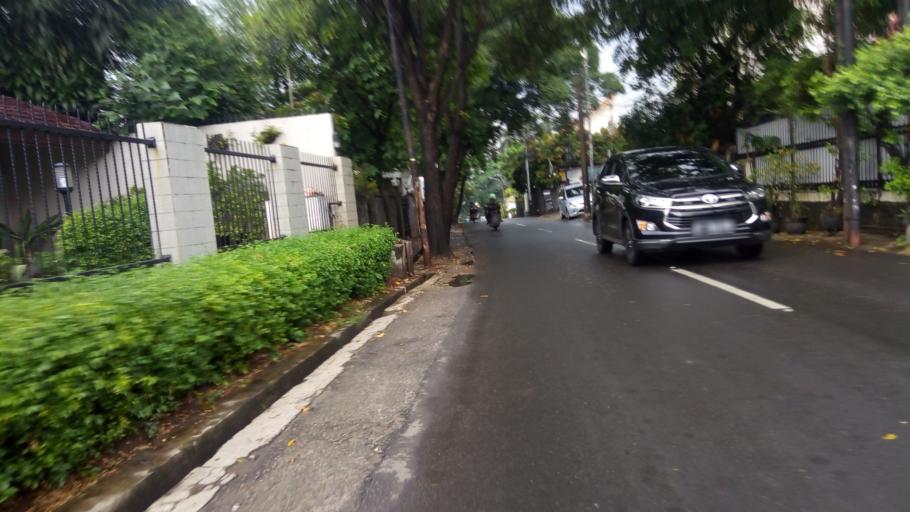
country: ID
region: Jakarta Raya
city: Jakarta
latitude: -6.2668
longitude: 106.8113
